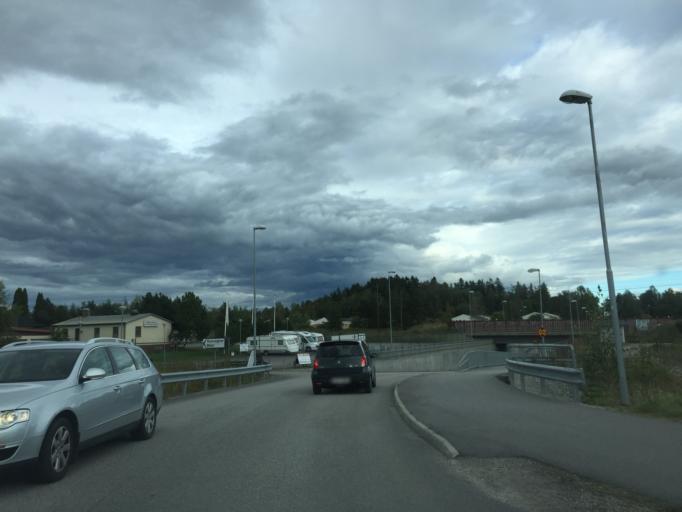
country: SE
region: OErebro
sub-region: Orebro Kommun
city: Hovsta
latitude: 59.3172
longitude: 15.2188
